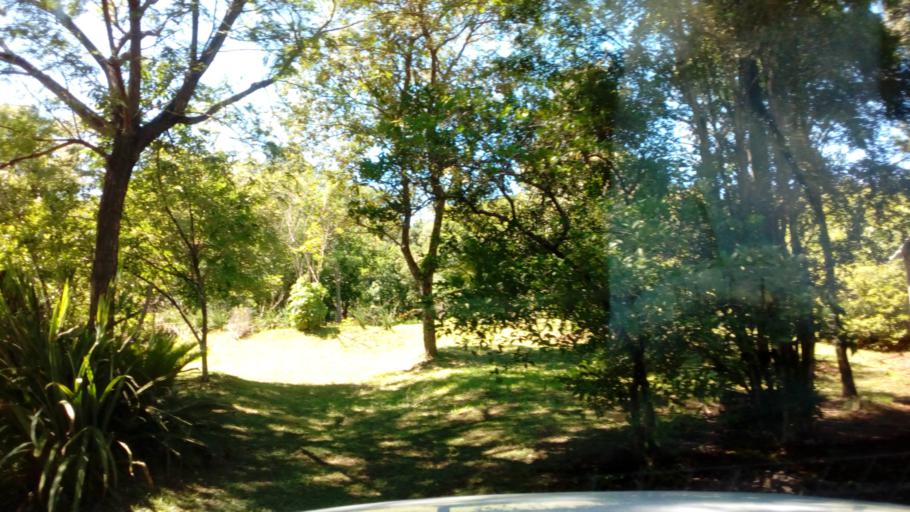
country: AR
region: Misiones
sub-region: Departamento de Leandro N. Alem
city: Leandro N. Alem
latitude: -27.5805
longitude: -55.3746
